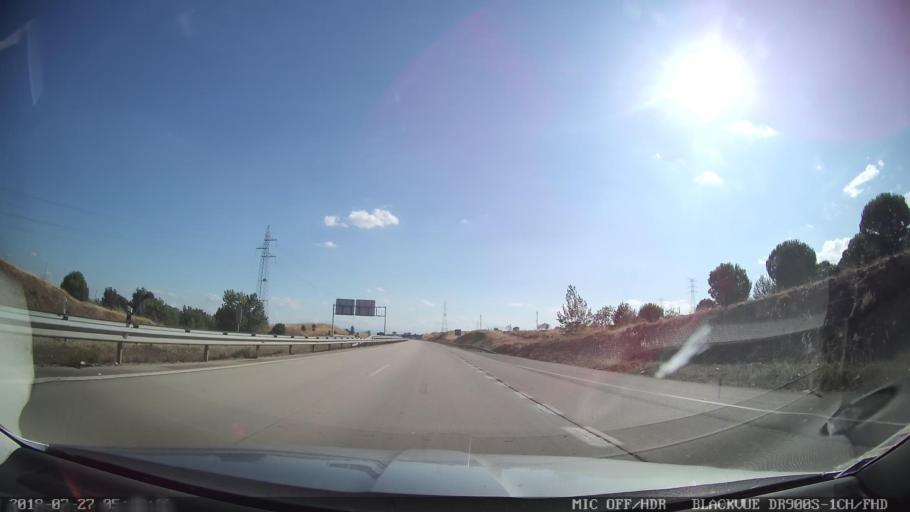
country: ES
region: Castille-La Mancha
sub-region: Province of Toledo
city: Talavera de la Reina
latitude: 39.9827
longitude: -4.8495
